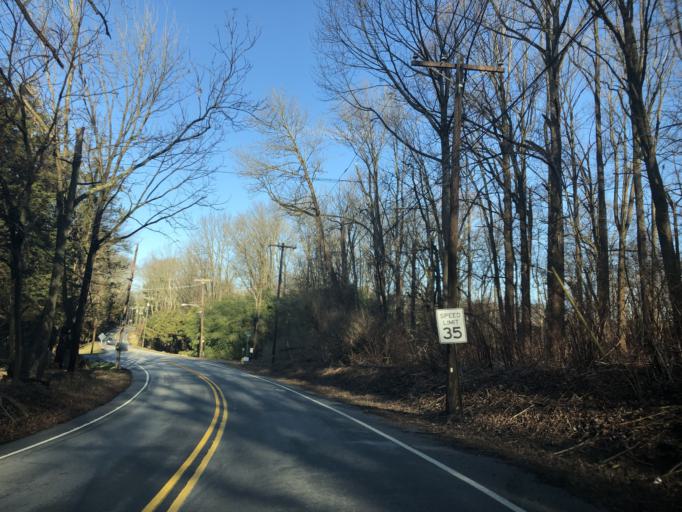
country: US
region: Pennsylvania
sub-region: Delaware County
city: Chester Heights
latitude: 39.8921
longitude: -75.4764
